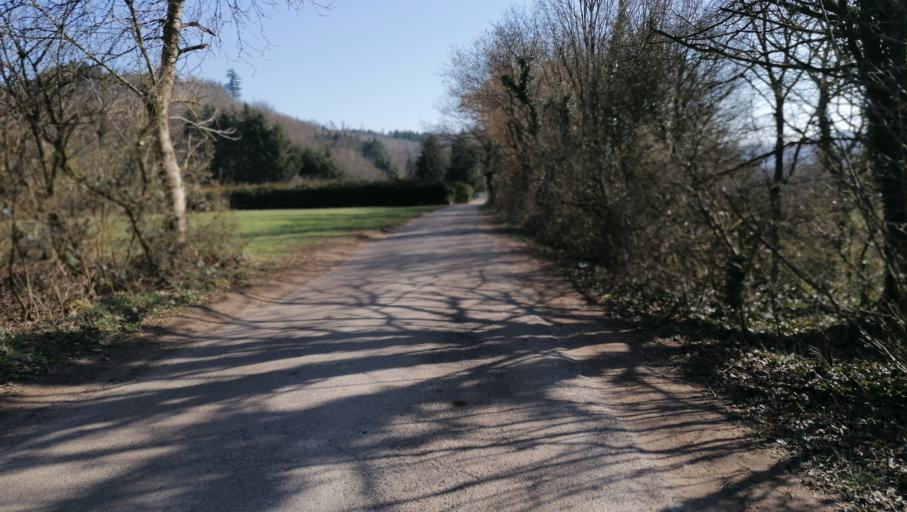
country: CH
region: Aargau
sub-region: Bezirk Rheinfelden
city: Mumpf
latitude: 47.5724
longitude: 7.9186
